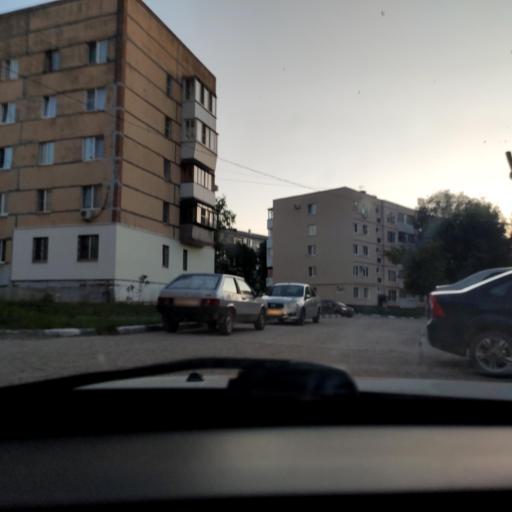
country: RU
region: Samara
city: Novokuybyshevsk
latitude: 53.0971
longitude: 49.9775
